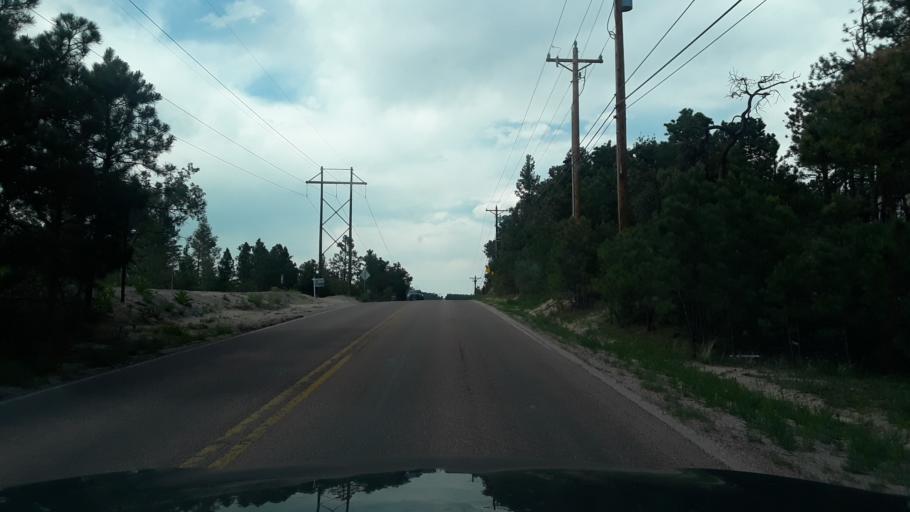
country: US
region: Colorado
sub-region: El Paso County
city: Gleneagle
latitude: 39.0491
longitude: -104.7848
